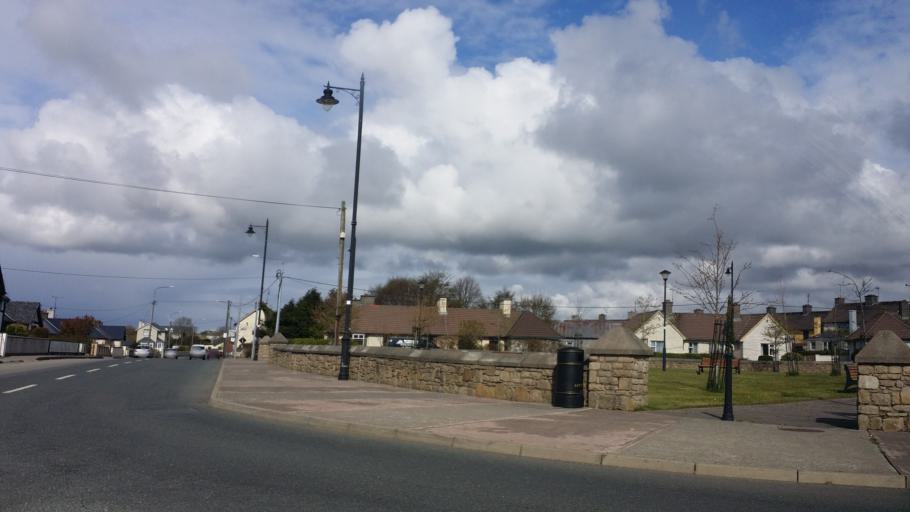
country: IE
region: Ulster
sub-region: County Donegal
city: Ballyshannon
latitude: 54.5046
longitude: -8.1909
